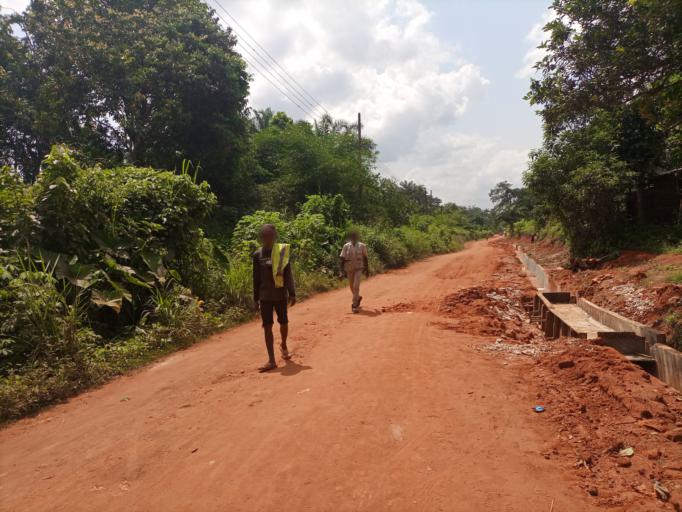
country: NG
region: Abia
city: Umuahia
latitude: 5.4816
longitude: 7.3304
